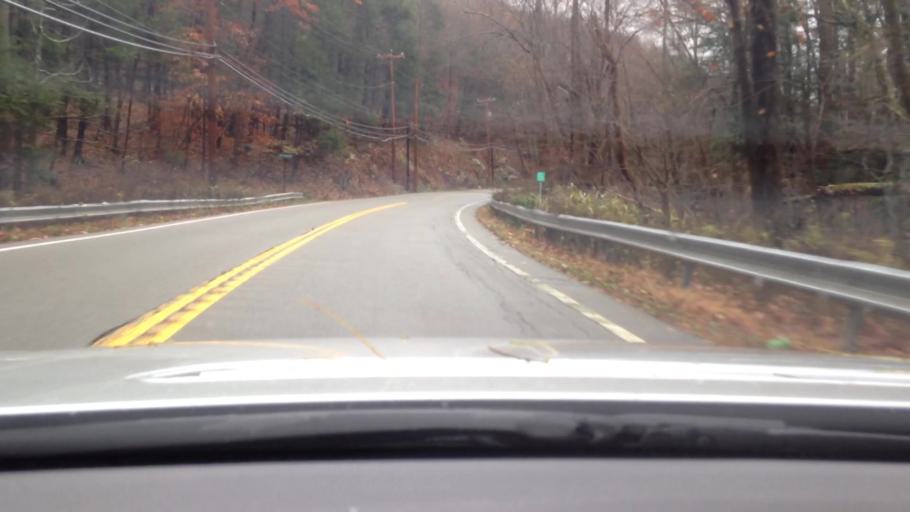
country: US
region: New York
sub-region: Orange County
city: Highland Falls
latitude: 41.3632
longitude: -73.9262
